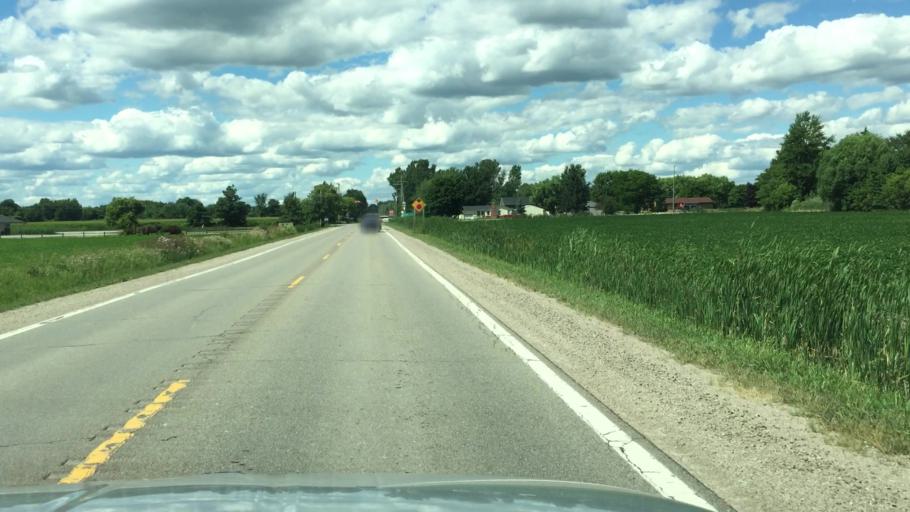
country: US
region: Michigan
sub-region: Macomb County
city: Romeo
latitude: 42.8472
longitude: -82.9643
